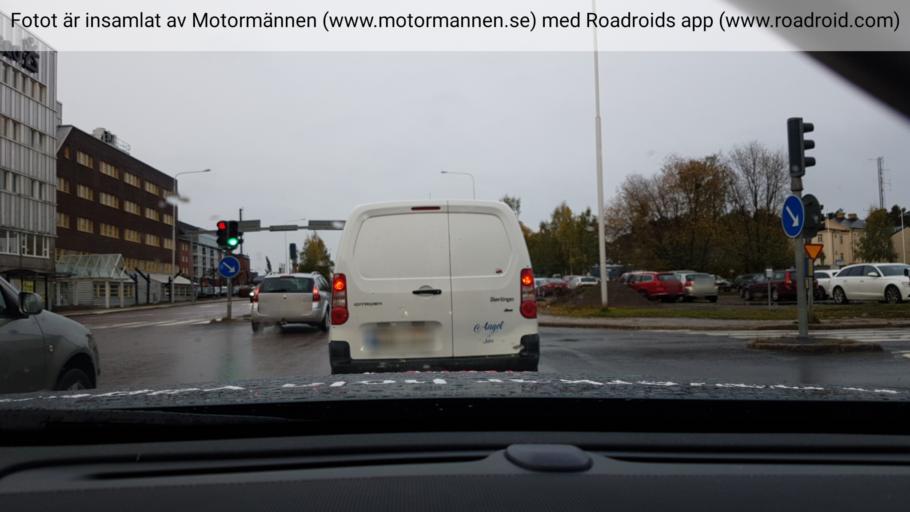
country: SE
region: Norrbotten
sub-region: Lulea Kommun
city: Lulea
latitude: 65.5802
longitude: 22.1385
